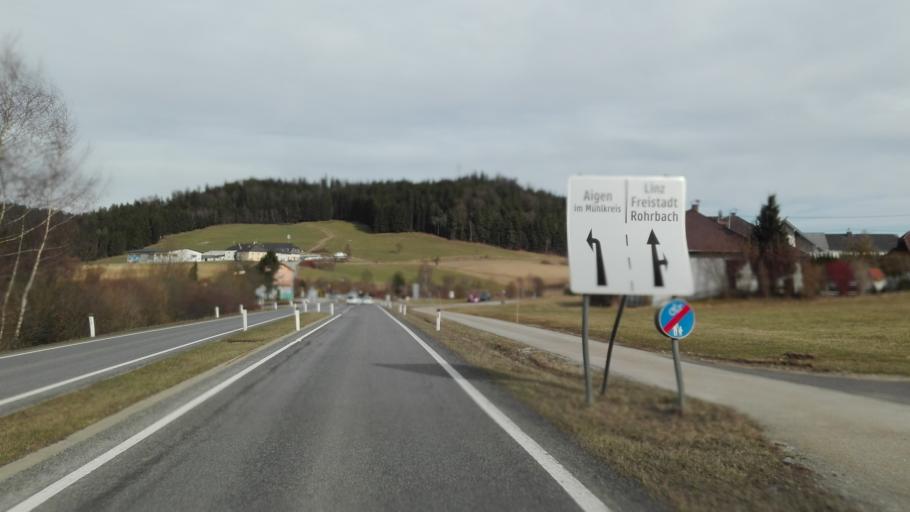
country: AT
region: Upper Austria
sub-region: Politischer Bezirk Rohrbach
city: Schlaegl
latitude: 48.5998
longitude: 13.9558
